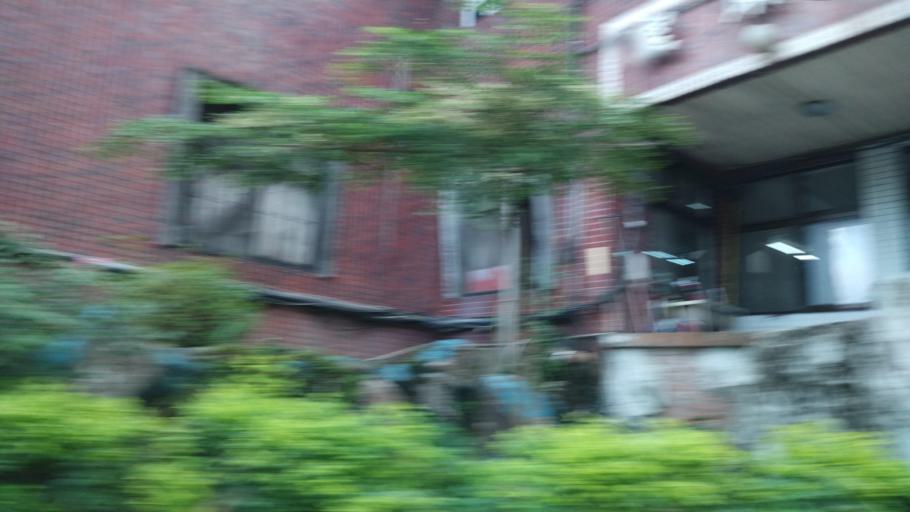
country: TW
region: Taipei
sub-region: Taipei
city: Banqiao
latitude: 24.9483
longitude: 121.4962
